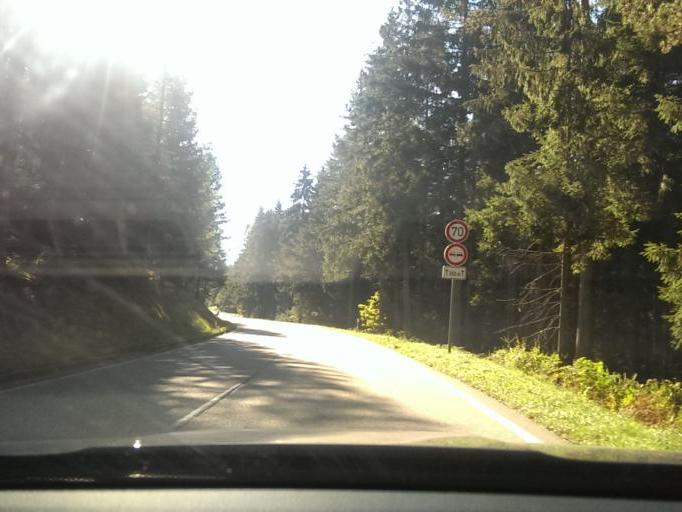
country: DE
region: Baden-Wuerttemberg
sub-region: Karlsruhe Region
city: Simmersfeld
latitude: 48.6451
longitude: 8.5111
